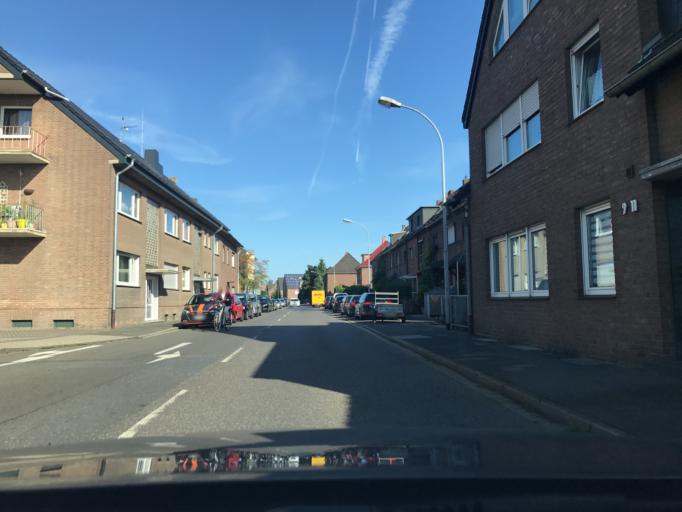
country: DE
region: North Rhine-Westphalia
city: Tonisvorst
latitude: 51.3225
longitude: 6.5014
